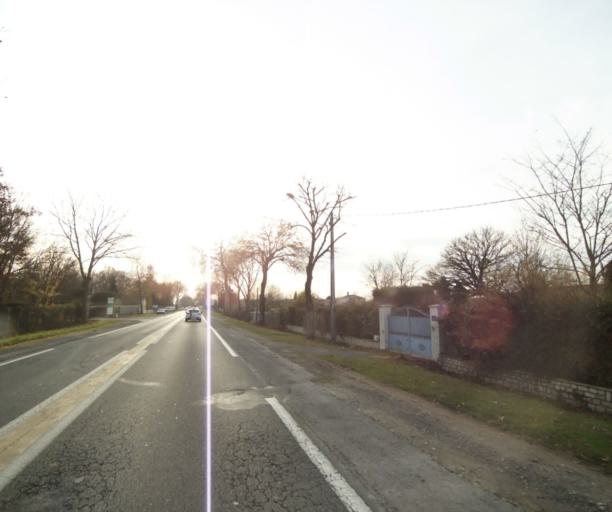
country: FR
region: Poitou-Charentes
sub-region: Departement de la Charente-Maritime
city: Fontcouverte
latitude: 45.7686
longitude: -0.5805
